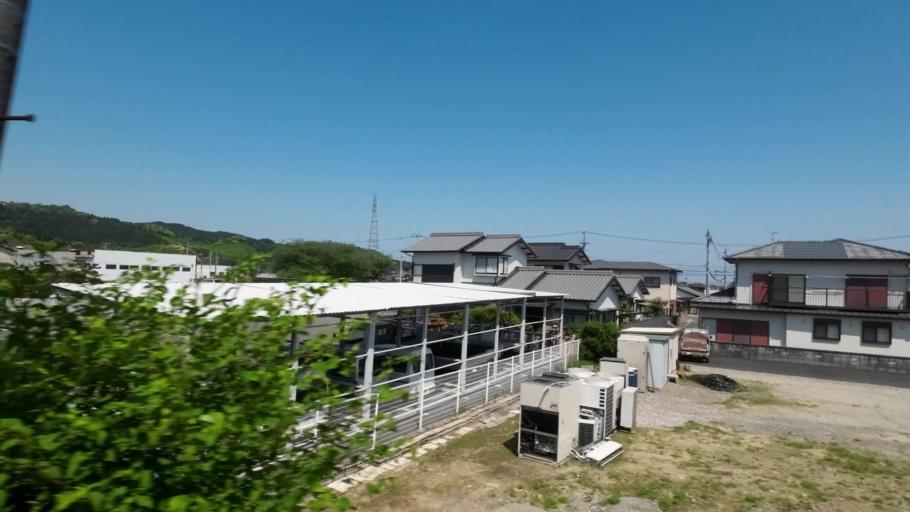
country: JP
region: Ehime
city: Niihama
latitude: 33.9427
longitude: 133.2887
